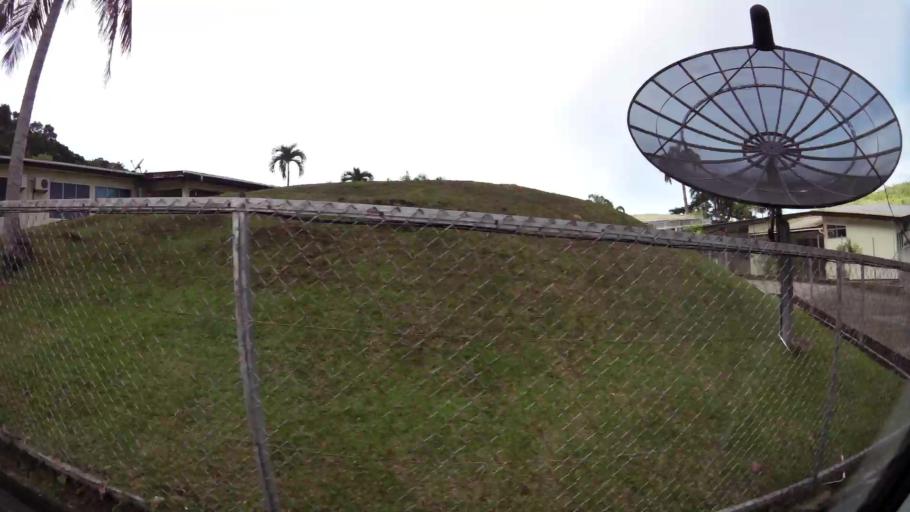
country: BN
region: Brunei and Muara
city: Bandar Seri Begawan
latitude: 4.9232
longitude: 115.0103
